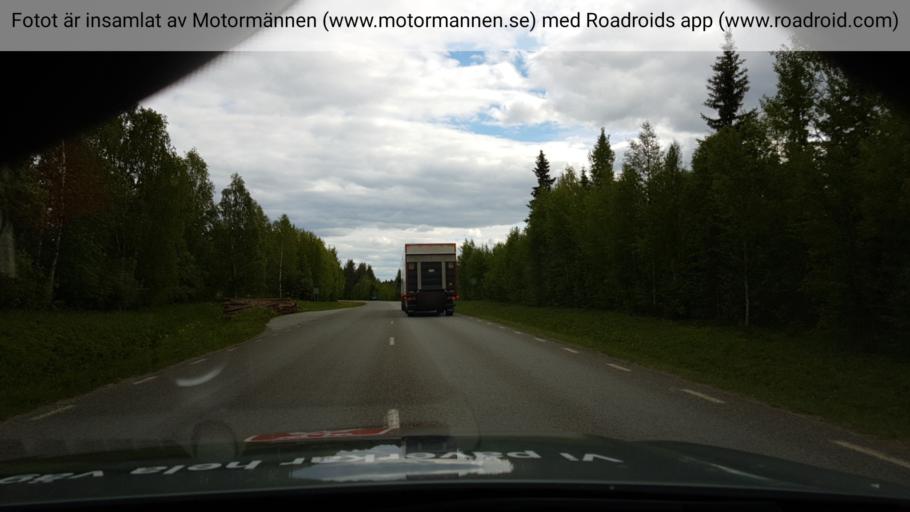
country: SE
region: Jaemtland
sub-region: Stroemsunds Kommun
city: Stroemsund
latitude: 63.8711
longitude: 15.5454
